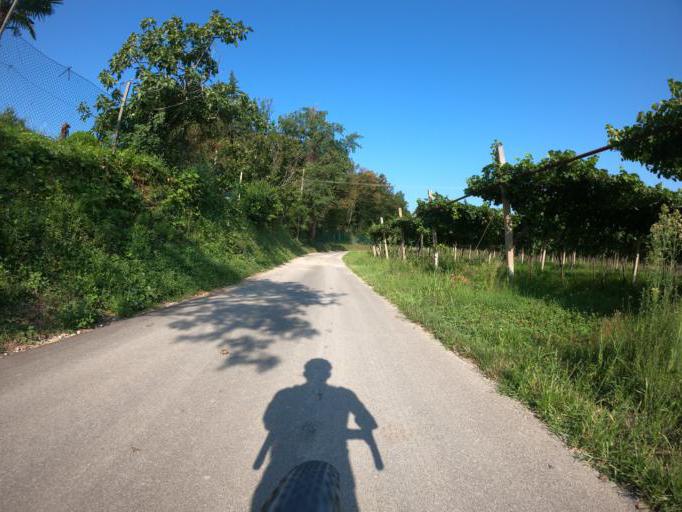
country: IT
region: Veneto
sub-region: Provincia di Verona
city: Calmasino
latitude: 45.5041
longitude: 10.7590
